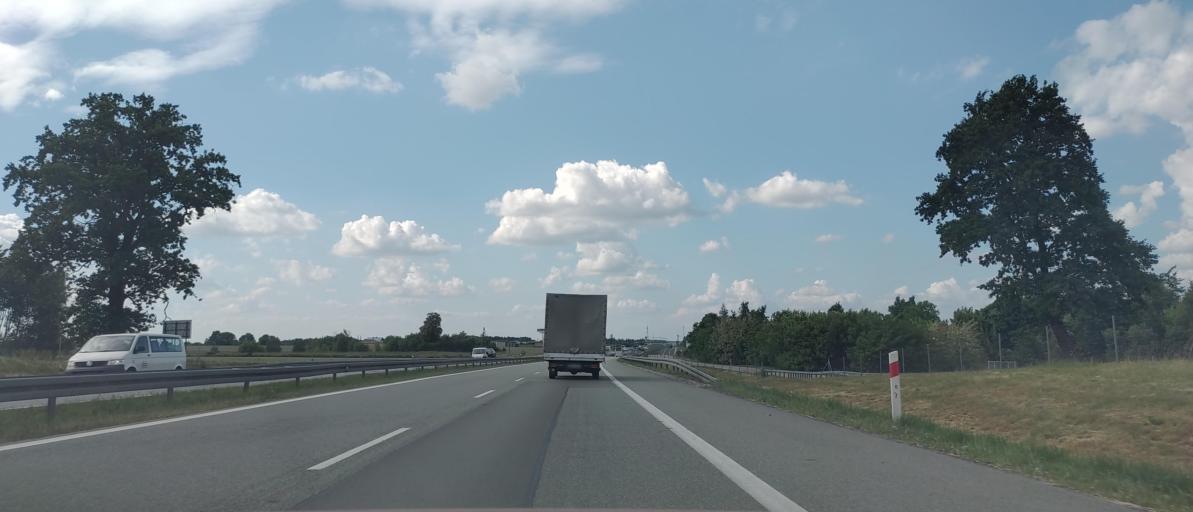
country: PL
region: Masovian Voivodeship
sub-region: Powiat bialobrzeski
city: Promna
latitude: 51.6833
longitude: 20.9362
